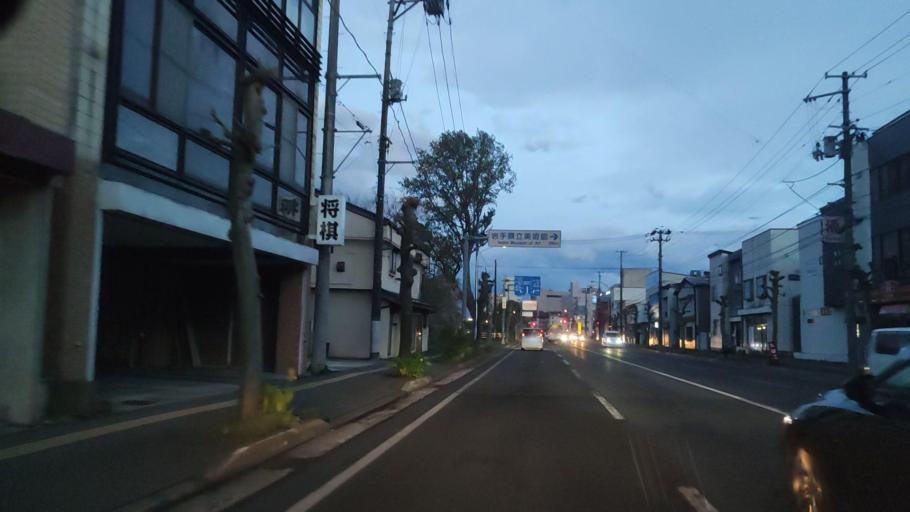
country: JP
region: Iwate
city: Morioka-shi
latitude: 39.7097
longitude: 141.1330
